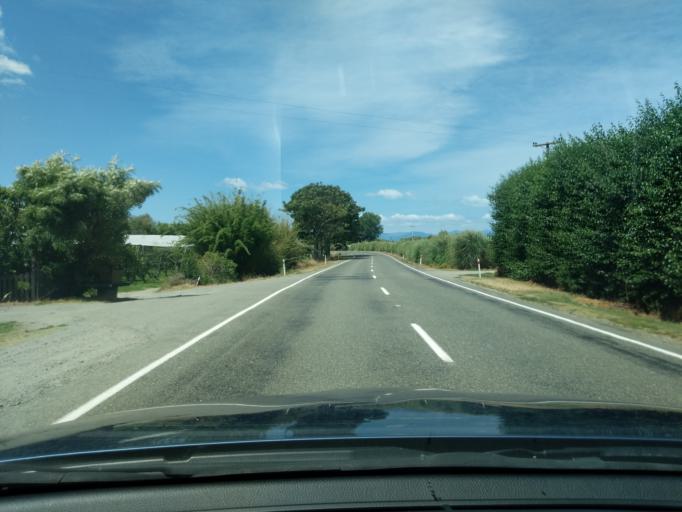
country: NZ
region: Tasman
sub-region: Tasman District
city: Motueka
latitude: -41.0606
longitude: 172.9734
